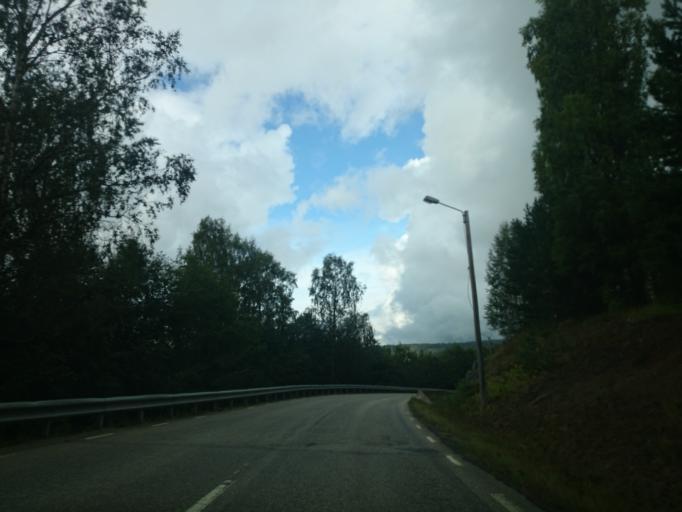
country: SE
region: Vaesternorrland
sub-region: Sundsvalls Kommun
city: Vi
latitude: 62.3098
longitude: 17.1788
